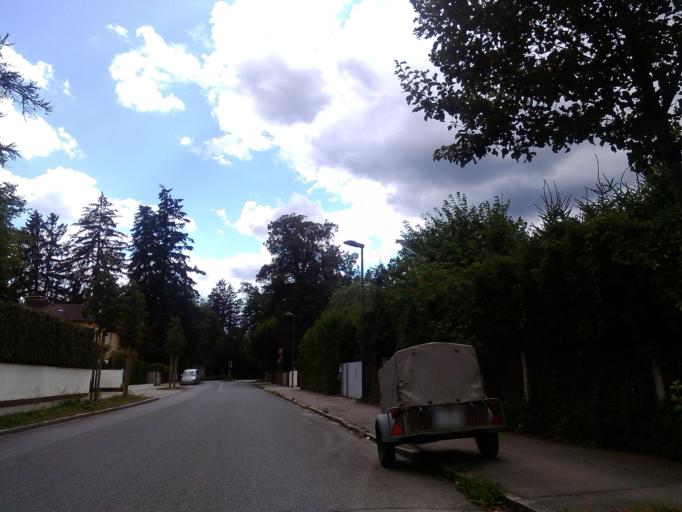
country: DE
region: Bavaria
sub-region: Upper Bavaria
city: Grafelfing
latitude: 48.1342
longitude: 11.4374
